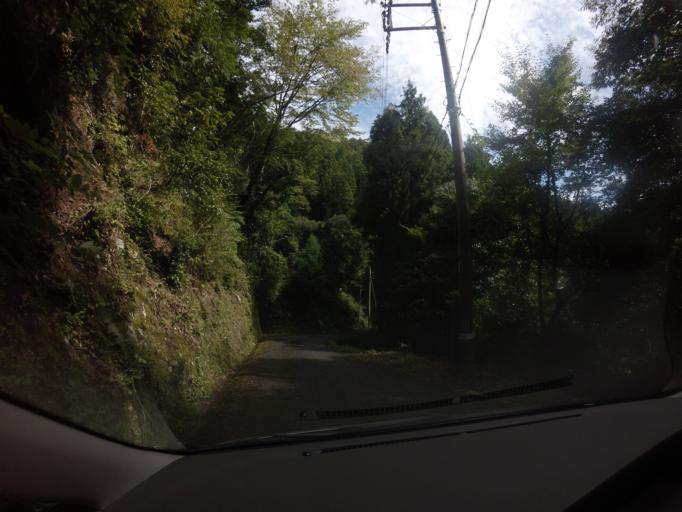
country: JP
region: Wakayama
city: Shingu
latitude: 33.9624
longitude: 135.8585
